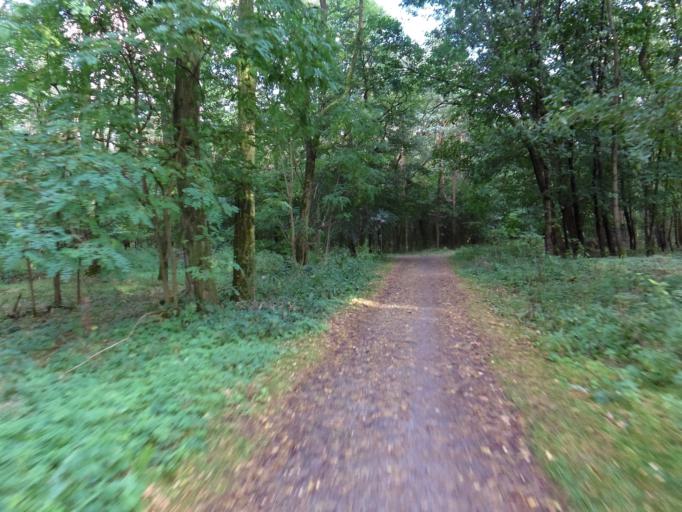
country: DE
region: Saxony-Anhalt
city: Schonebeck
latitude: 52.0698
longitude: 11.7130
